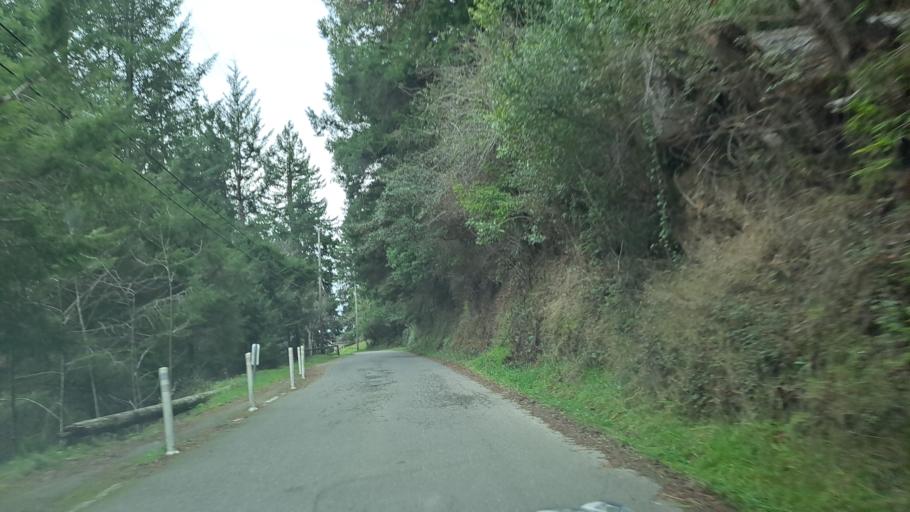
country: US
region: California
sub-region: Humboldt County
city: Fortuna
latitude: 40.6021
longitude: -124.1522
